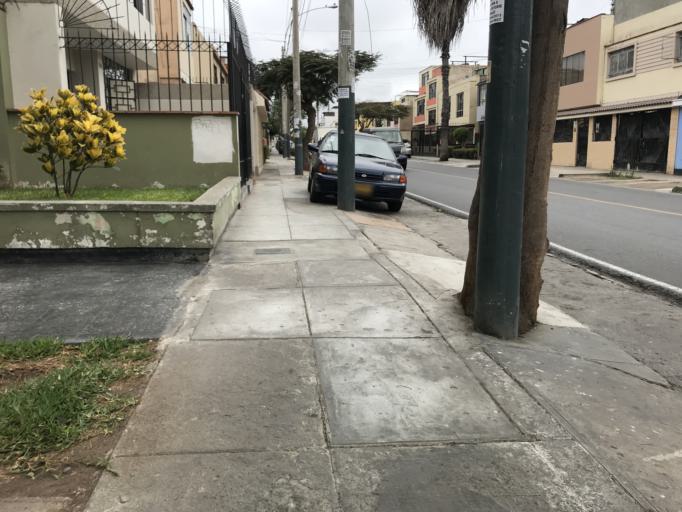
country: PE
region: Lima
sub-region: Lima
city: San Isidro
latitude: -12.0742
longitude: -77.0726
